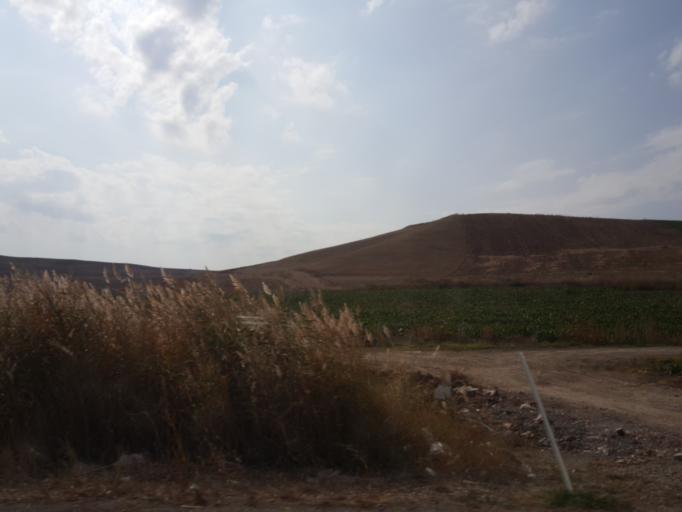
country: TR
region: Corum
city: Alaca
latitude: 40.1747
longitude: 34.8848
